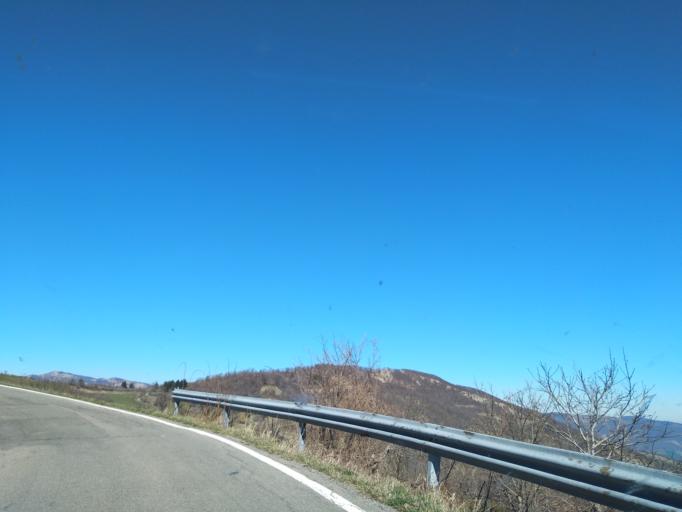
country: IT
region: Emilia-Romagna
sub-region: Provincia di Reggio Emilia
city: Ramiseto
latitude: 44.4065
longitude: 10.2693
